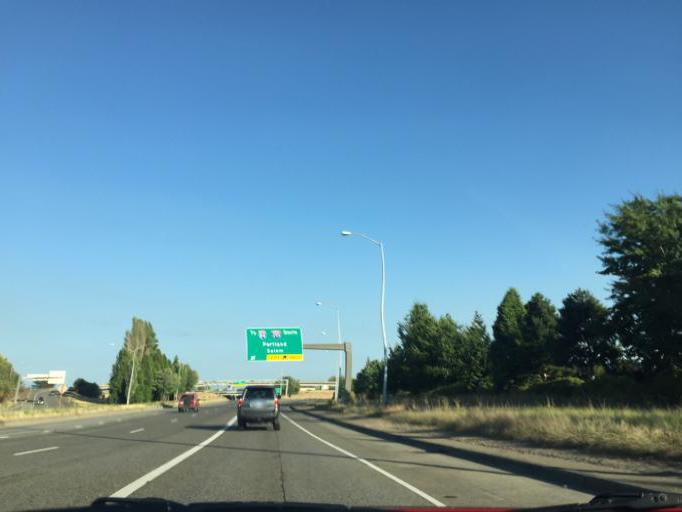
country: US
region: Washington
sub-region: Clark County
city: Mill Plain
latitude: 45.5738
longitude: -122.5550
